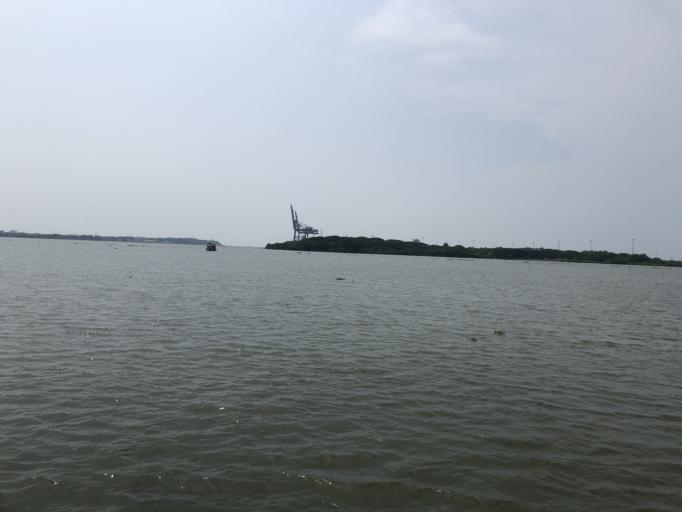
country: IN
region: Kerala
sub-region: Ernakulam
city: Cochin
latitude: 9.9843
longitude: 76.2651
